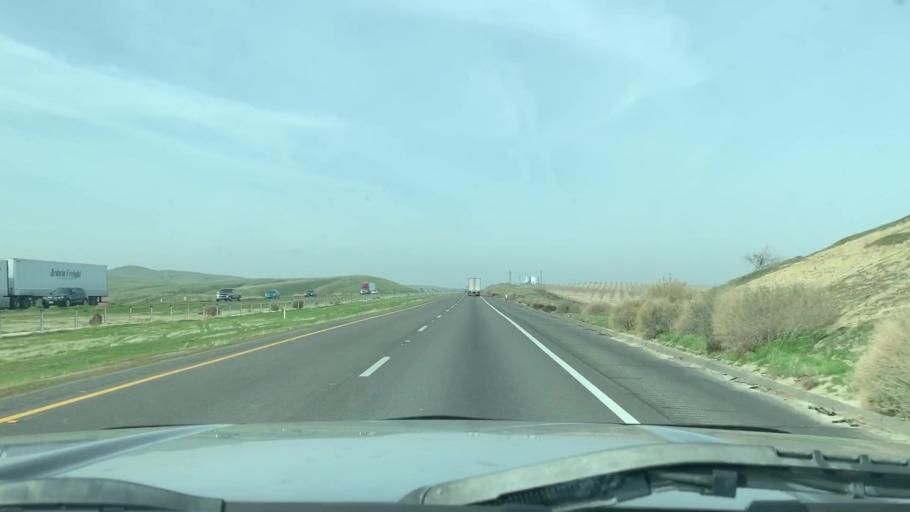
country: US
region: California
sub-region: Kings County
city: Kettleman City
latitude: 36.0405
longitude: -120.0404
